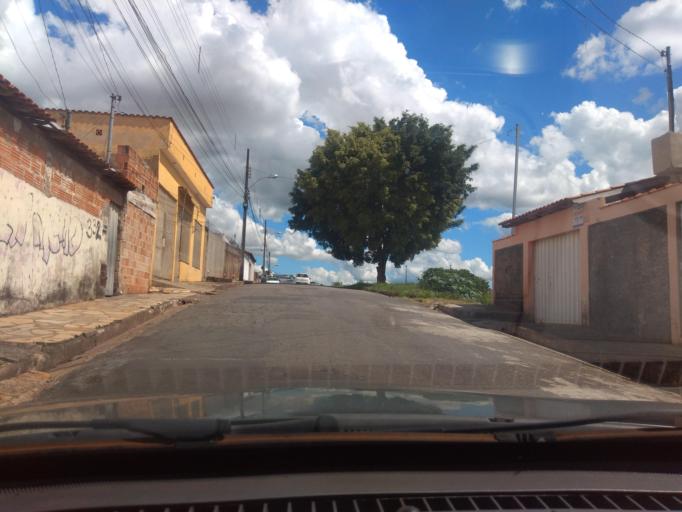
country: BR
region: Minas Gerais
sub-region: Tres Coracoes
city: Tres Coracoes
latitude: -21.6828
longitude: -45.2504
